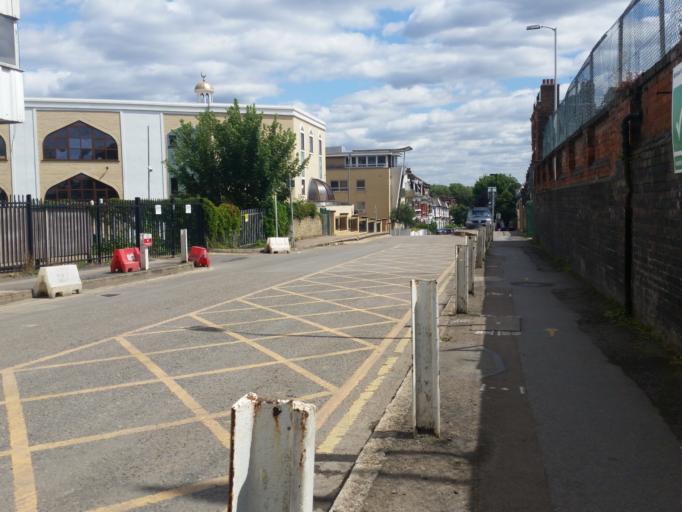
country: GB
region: England
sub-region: Greater London
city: Harringay
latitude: 51.5870
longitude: -0.1099
